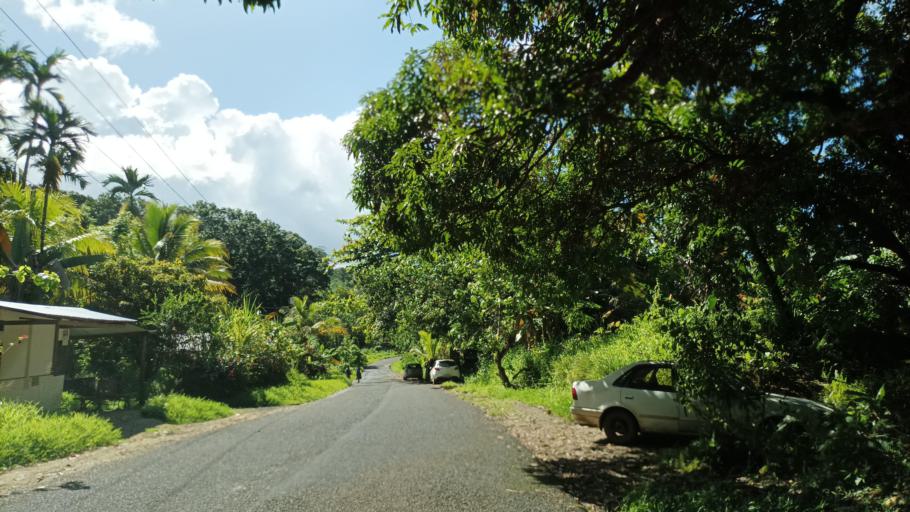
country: FM
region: Pohnpei
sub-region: Madolenihm Municipality
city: Madolenihm Municipality Government
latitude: 6.8499
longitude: 158.2992
